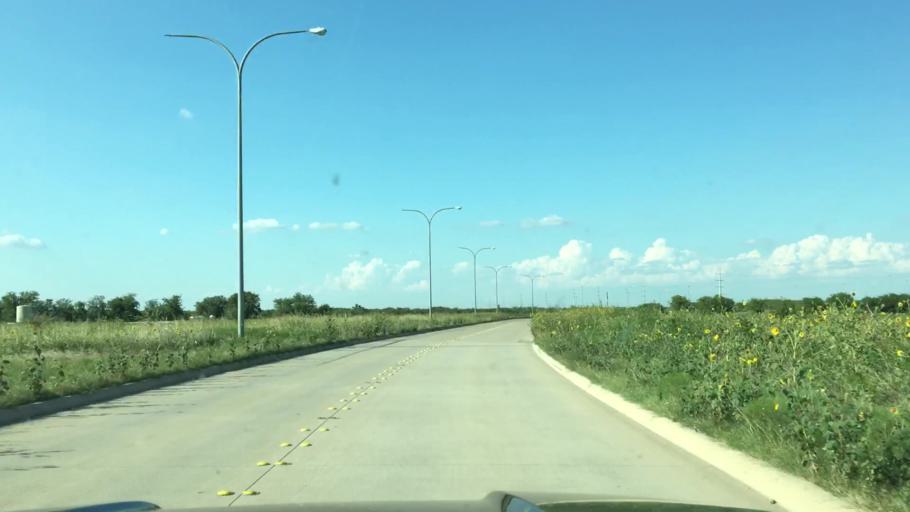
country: US
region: Texas
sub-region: Tarrant County
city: Haslet
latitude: 33.0050
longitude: -97.3587
